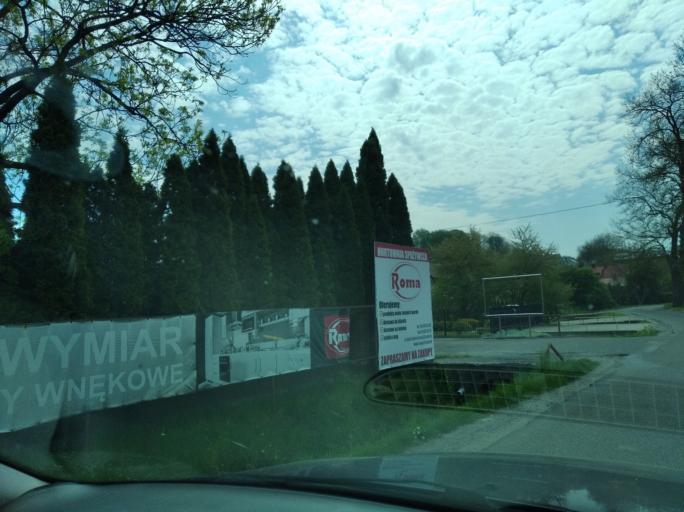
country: PL
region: Subcarpathian Voivodeship
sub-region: Powiat jaroslawski
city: Jaroslaw
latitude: 50.0153
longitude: 22.6646
